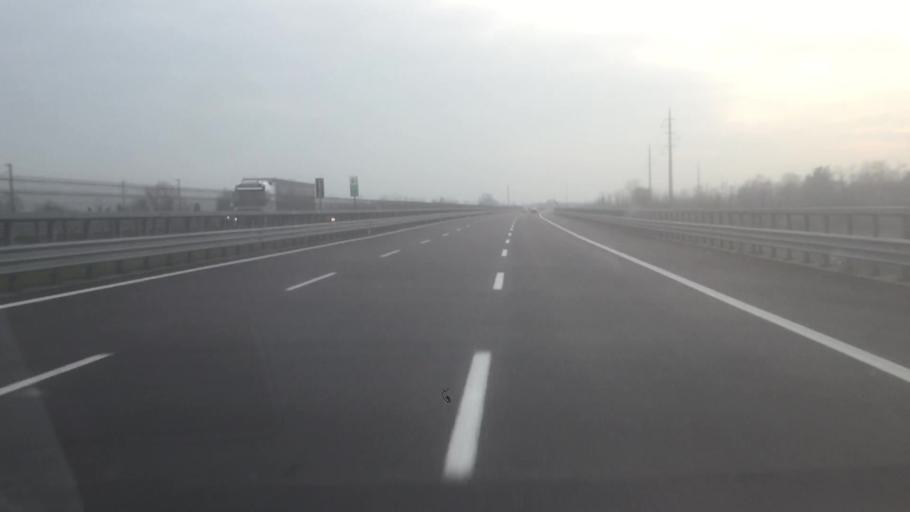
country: IT
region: Lombardy
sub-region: Provincia di Brescia
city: Urago d'Oglio
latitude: 45.4992
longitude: 9.8653
